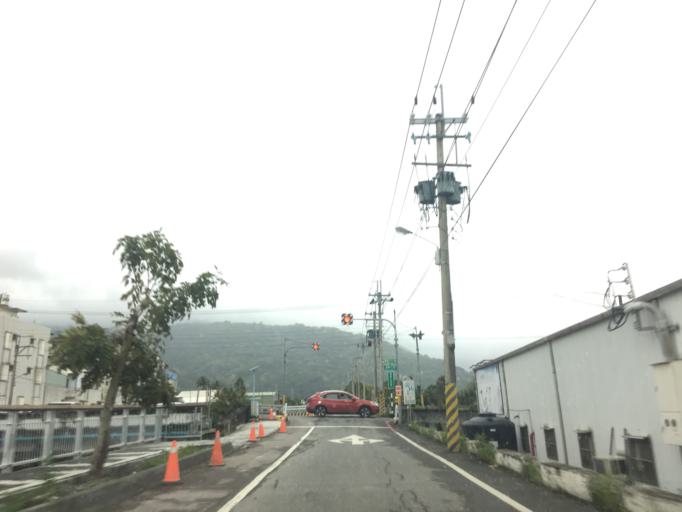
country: TW
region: Taiwan
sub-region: Hualien
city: Hualian
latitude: 23.9844
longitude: 121.5677
